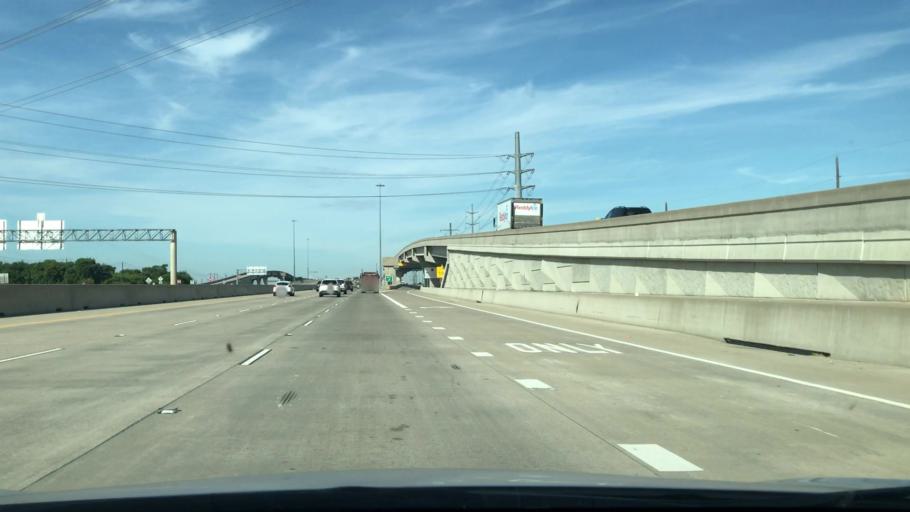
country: US
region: Texas
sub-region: Collin County
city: Fairview
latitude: 33.1543
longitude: -96.6546
